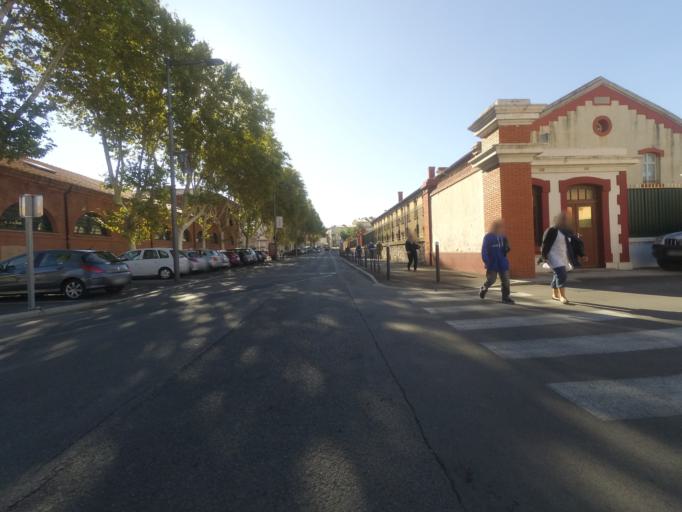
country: FR
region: Languedoc-Roussillon
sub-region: Departement des Pyrenees-Orientales
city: Perpignan
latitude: 42.6956
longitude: 2.9002
